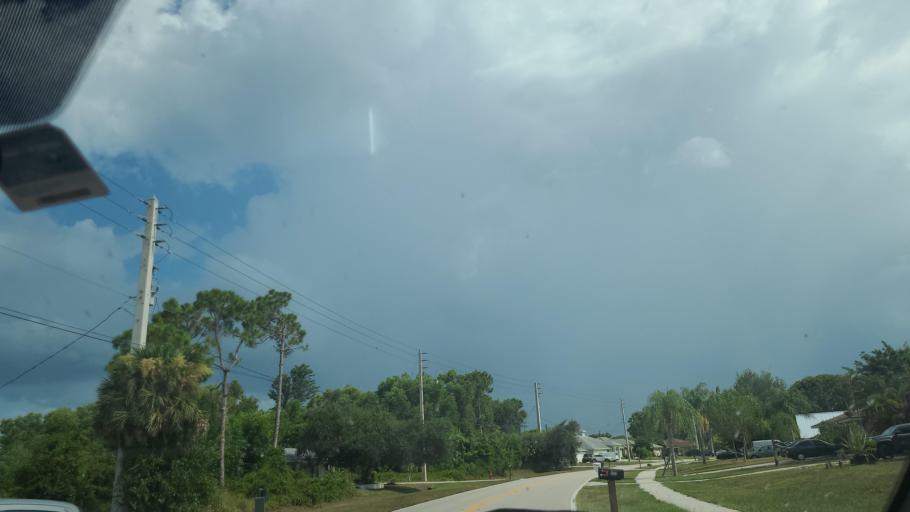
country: US
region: Florida
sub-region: Saint Lucie County
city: Port Saint Lucie
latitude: 27.2548
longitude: -80.3541
